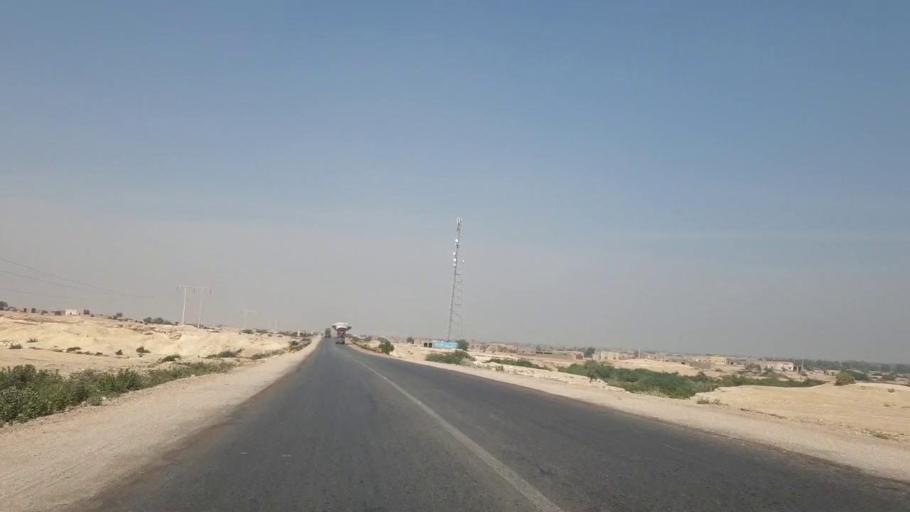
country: PK
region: Sindh
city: Hala
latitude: 25.7712
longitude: 68.2862
